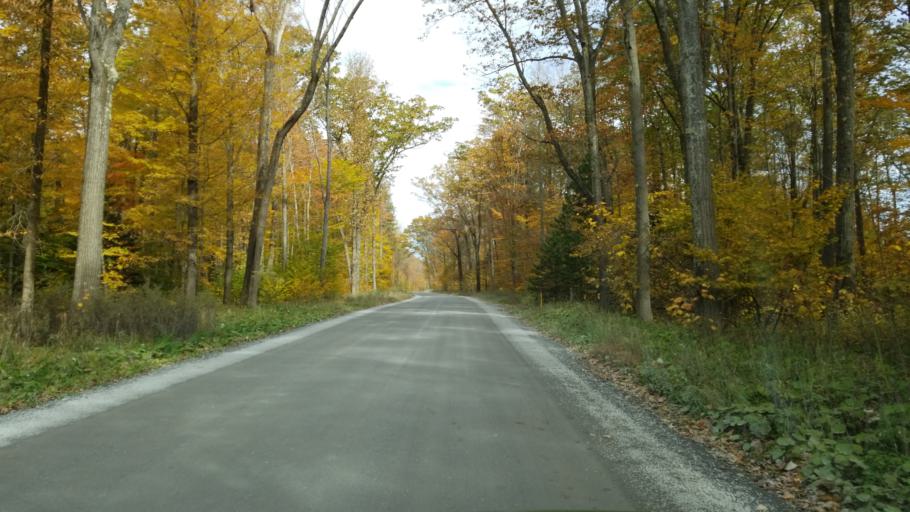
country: US
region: Pennsylvania
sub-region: Clearfield County
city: Clearfield
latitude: 41.1301
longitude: -78.5260
